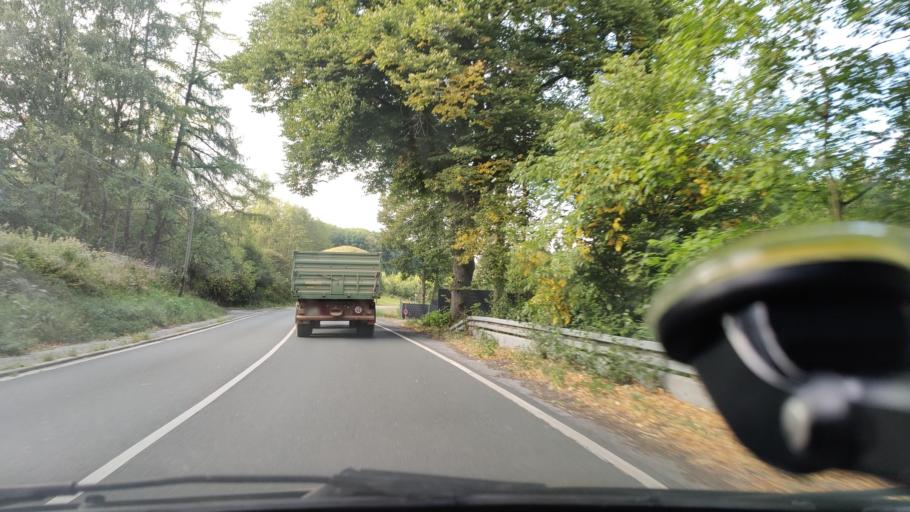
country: DE
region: North Rhine-Westphalia
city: Schwerte
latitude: 51.3863
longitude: 7.5871
